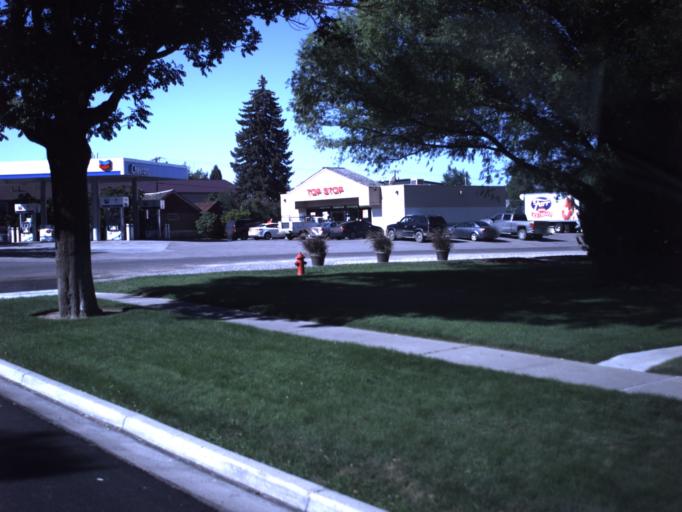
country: US
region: Utah
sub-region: Sanpete County
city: Manti
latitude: 39.2701
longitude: -111.6371
